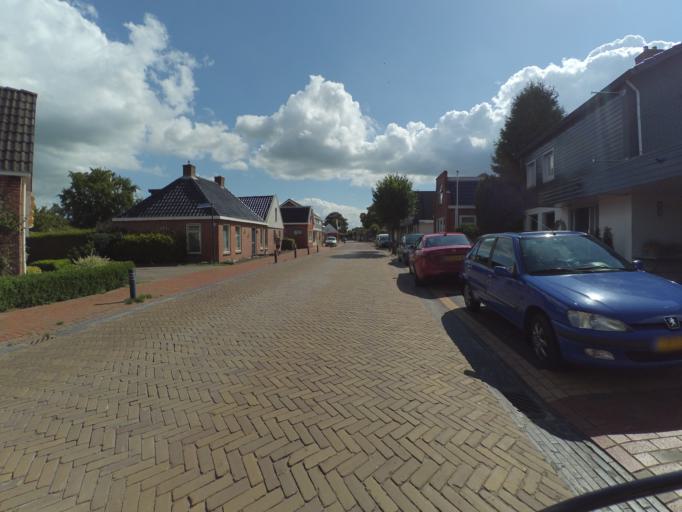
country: NL
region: Friesland
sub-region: Gemeente Achtkarspelen
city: Drogeham
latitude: 53.2025
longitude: 6.1128
